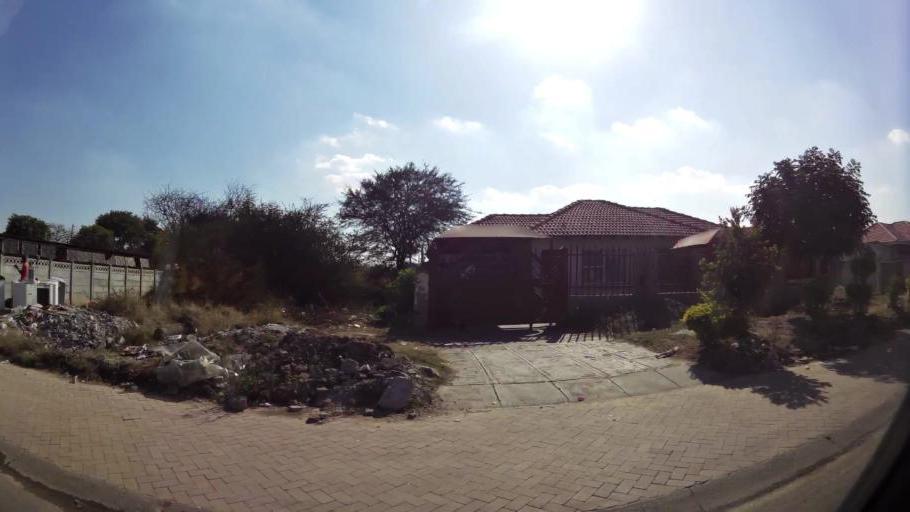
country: ZA
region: North-West
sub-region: Bojanala Platinum District Municipality
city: Rustenburg
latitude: -25.6603
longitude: 27.2314
